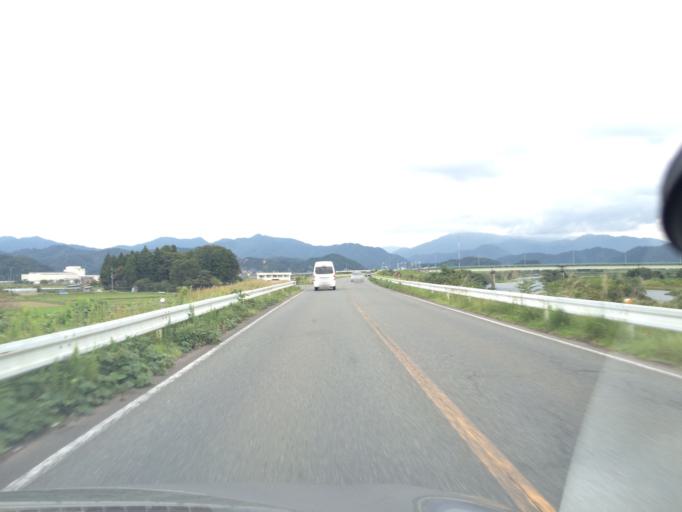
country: JP
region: Hyogo
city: Toyooka
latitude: 35.5103
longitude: 134.8305
